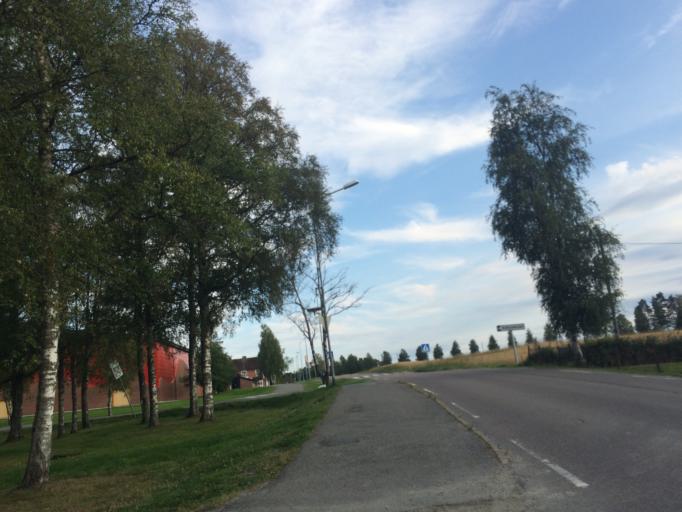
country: NO
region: Akershus
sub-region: Ski
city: Ski
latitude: 59.6795
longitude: 10.8840
